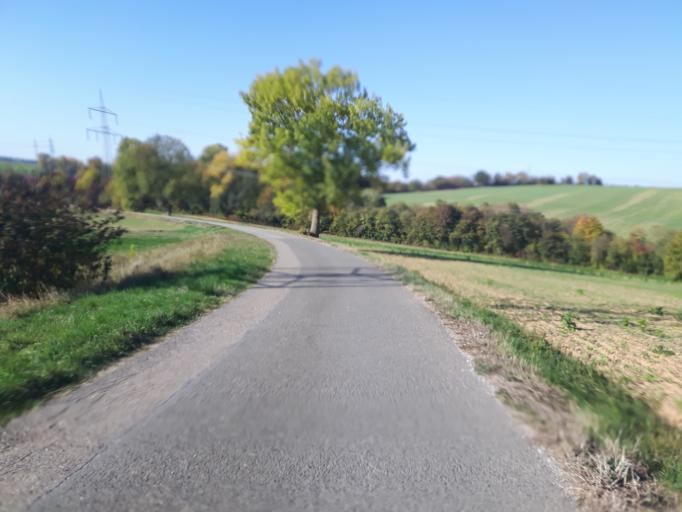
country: DE
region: Baden-Wuerttemberg
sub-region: Regierungsbezirk Stuttgart
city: Leingarten
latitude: 49.1598
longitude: 9.1540
